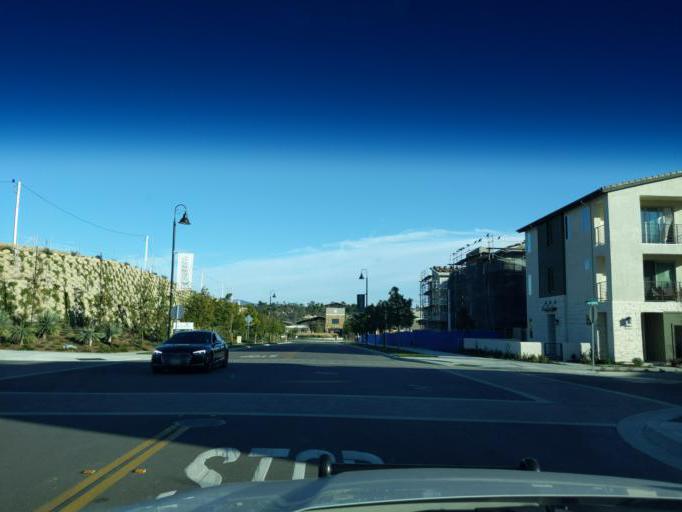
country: US
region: California
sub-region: Orange County
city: Lake Forest
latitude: 33.6603
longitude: -117.6818
